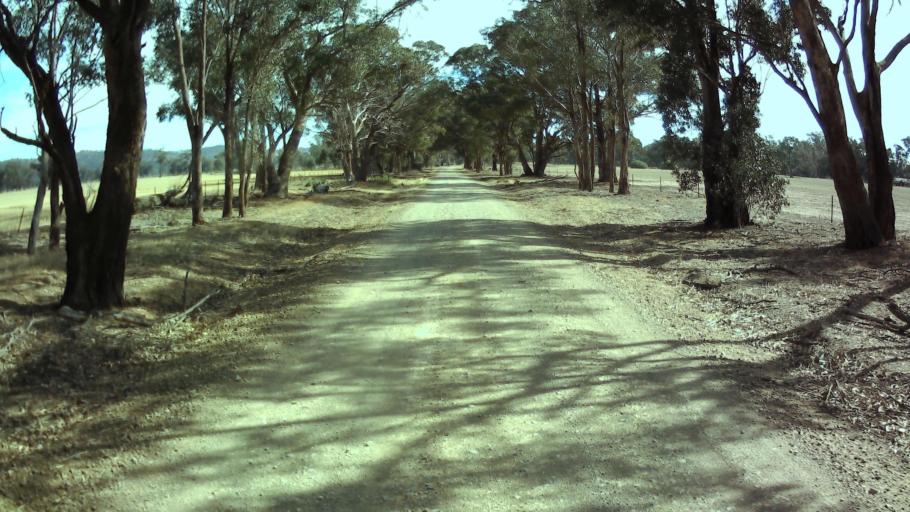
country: AU
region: New South Wales
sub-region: Weddin
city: Grenfell
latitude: -33.6970
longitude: 148.3028
